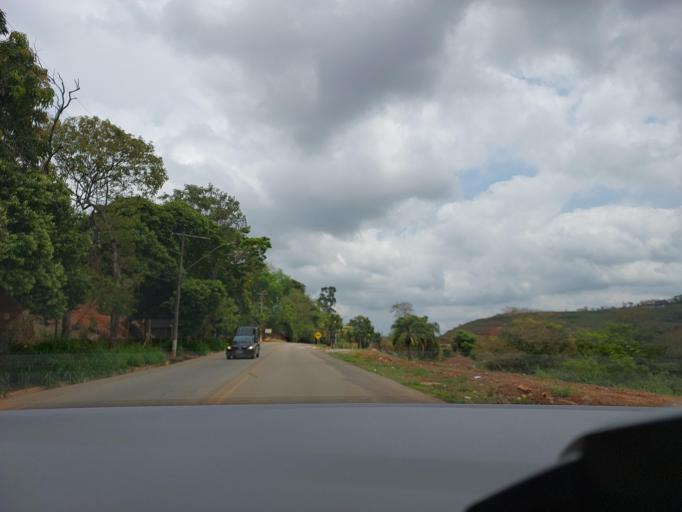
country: BR
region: Minas Gerais
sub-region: Ponte Nova
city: Ponte Nova
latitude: -20.3989
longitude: -42.8814
